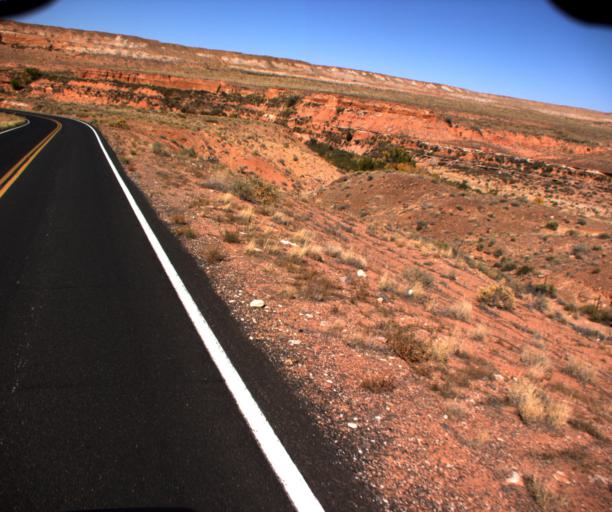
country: US
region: Arizona
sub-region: Coconino County
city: Tuba City
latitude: 36.0999
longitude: -111.1955
